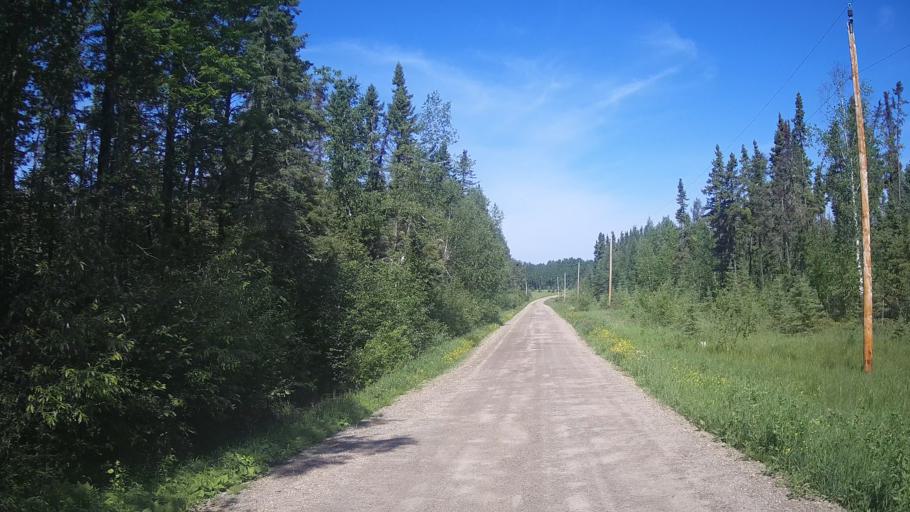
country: CA
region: Ontario
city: Dryden
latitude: 49.8177
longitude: -93.3320
